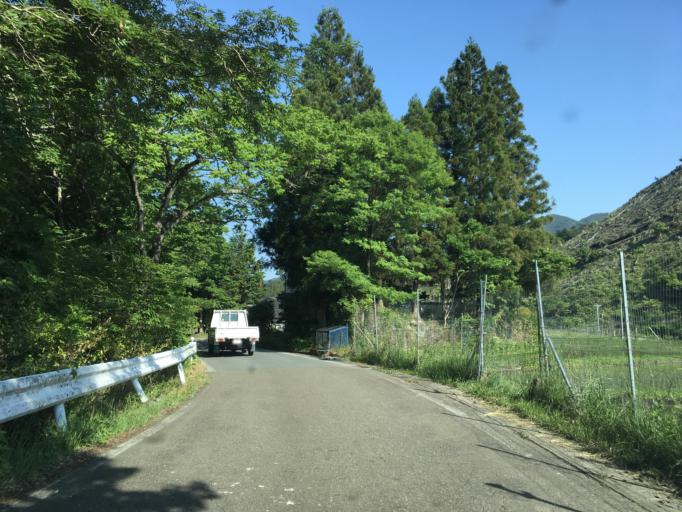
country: JP
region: Iwate
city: Kamaishi
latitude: 39.1952
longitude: 141.8383
